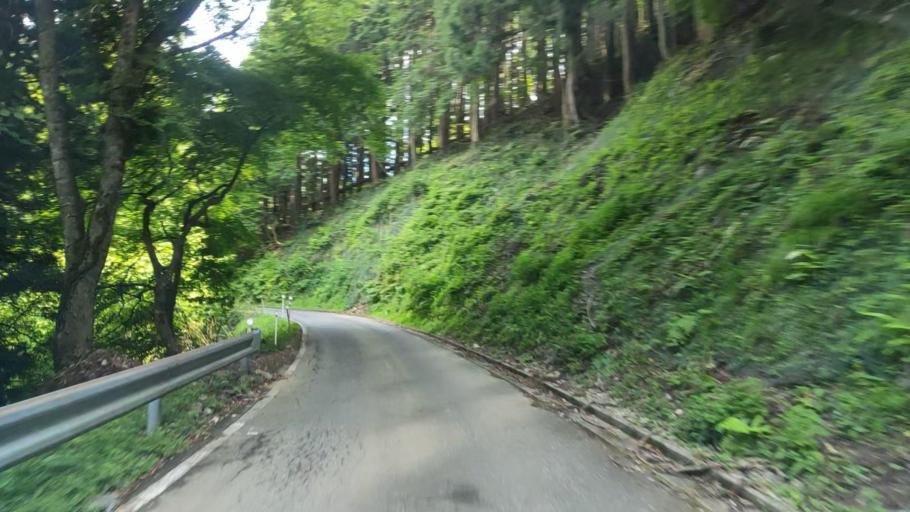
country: JP
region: Fukui
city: Ono
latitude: 35.7123
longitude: 136.5825
